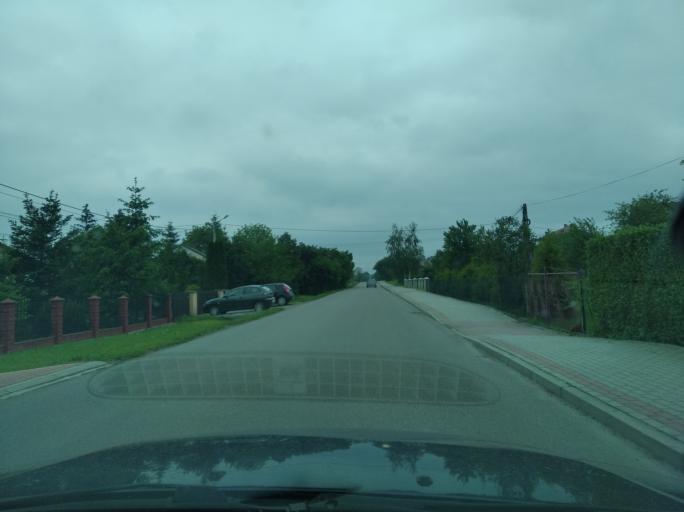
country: PL
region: Subcarpathian Voivodeship
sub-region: Powiat ropczycko-sedziszowski
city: Sedziszow Malopolski
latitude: 50.0791
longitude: 21.6749
